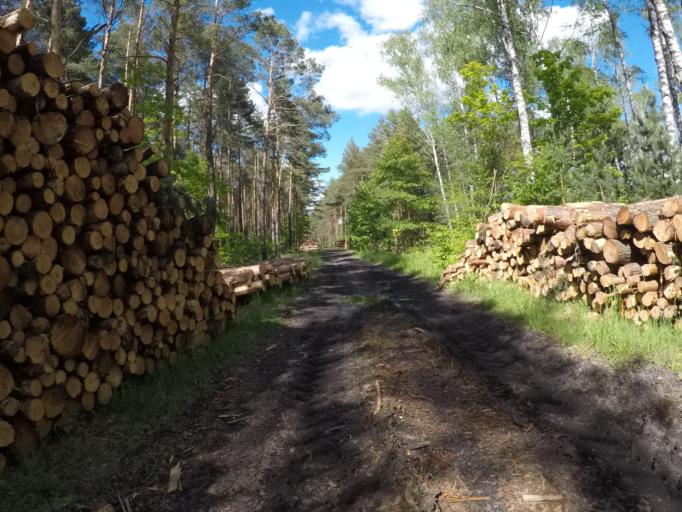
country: PL
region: Swietokrzyskie
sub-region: Powiat kielecki
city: Kostomloty Drugie
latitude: 50.8862
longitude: 20.5352
